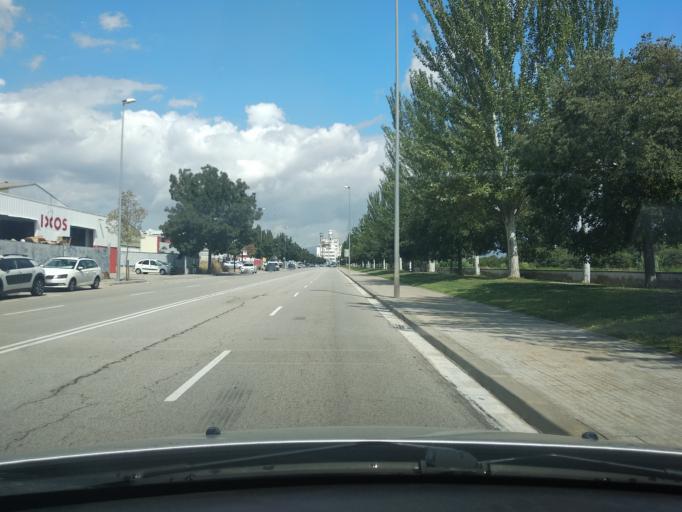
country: ES
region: Catalonia
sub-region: Provincia de Barcelona
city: Granollers
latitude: 41.6037
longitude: 2.2789
